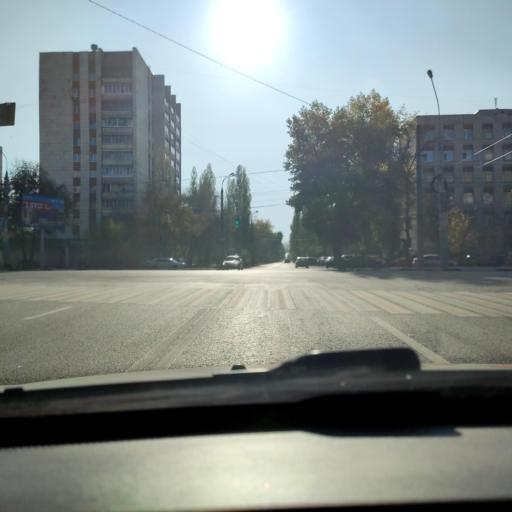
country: RU
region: Voronezj
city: Voronezh
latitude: 51.6716
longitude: 39.2561
